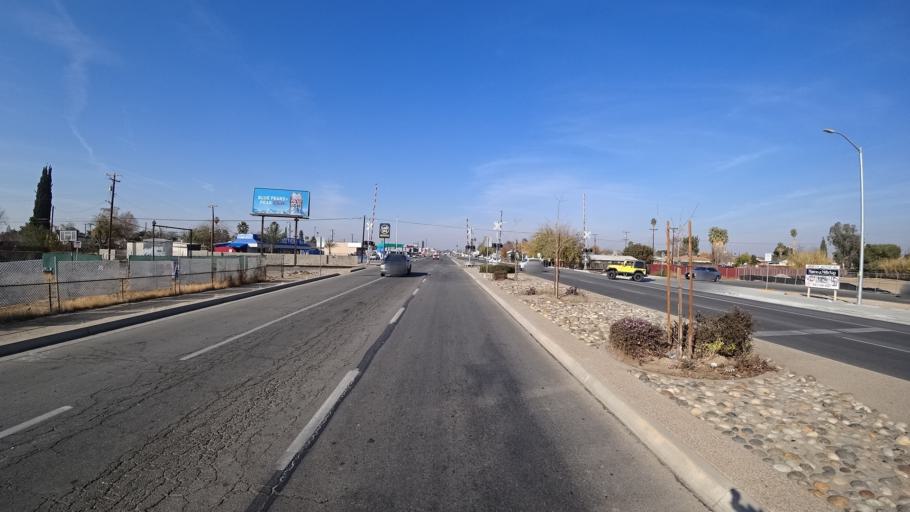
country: US
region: California
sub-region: Kern County
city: Bakersfield
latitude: 35.3295
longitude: -119.0124
